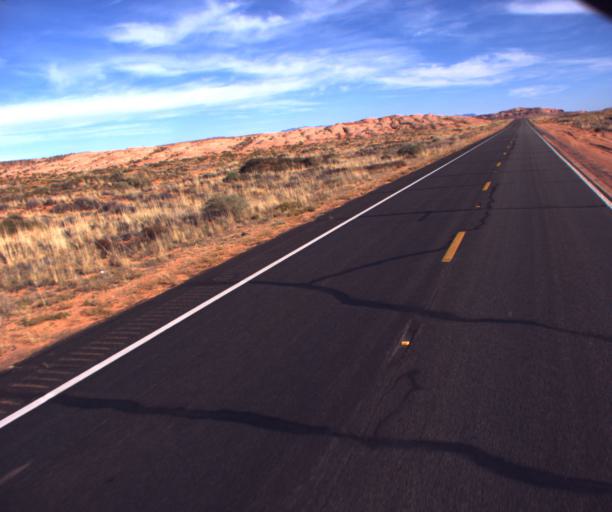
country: US
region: Arizona
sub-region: Apache County
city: Many Farms
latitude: 36.9363
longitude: -109.6347
